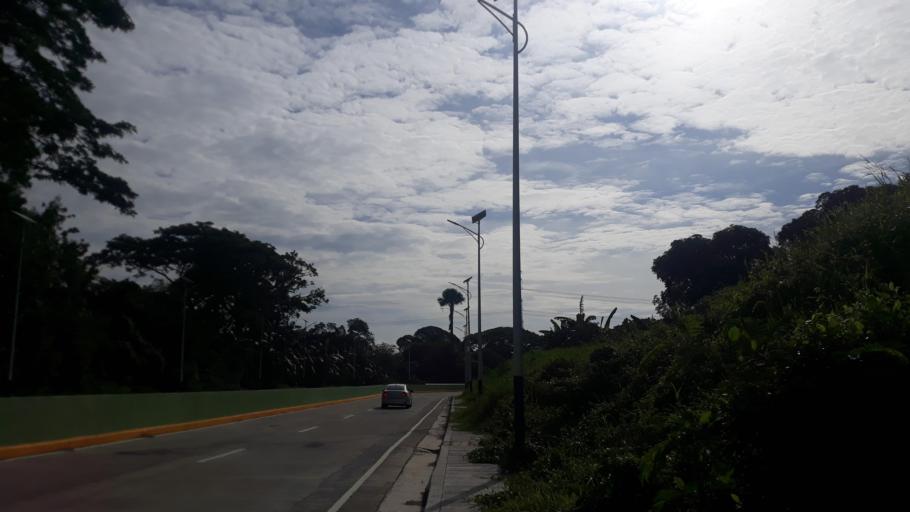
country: PH
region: Calabarzon
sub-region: Province of Cavite
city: Bulihan
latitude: 14.2891
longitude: 120.9650
